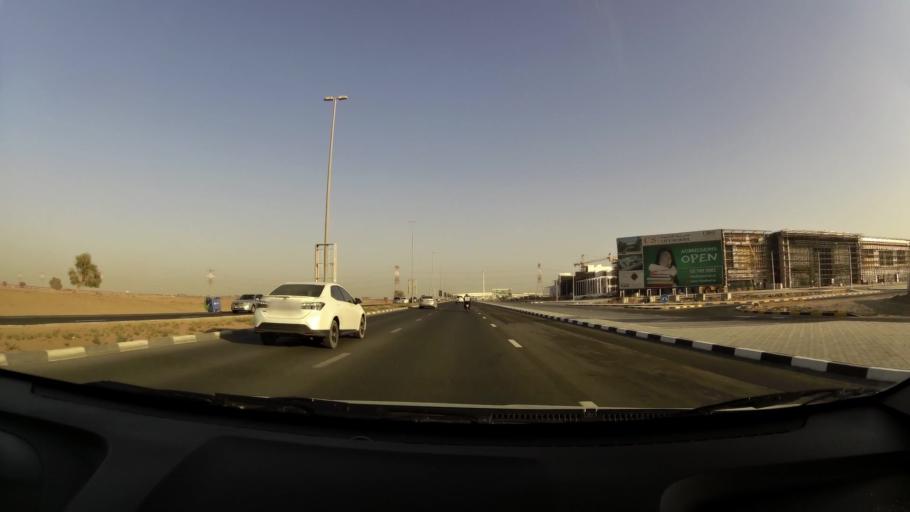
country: AE
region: Ajman
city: Ajman
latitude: 25.3674
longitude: 55.5113
